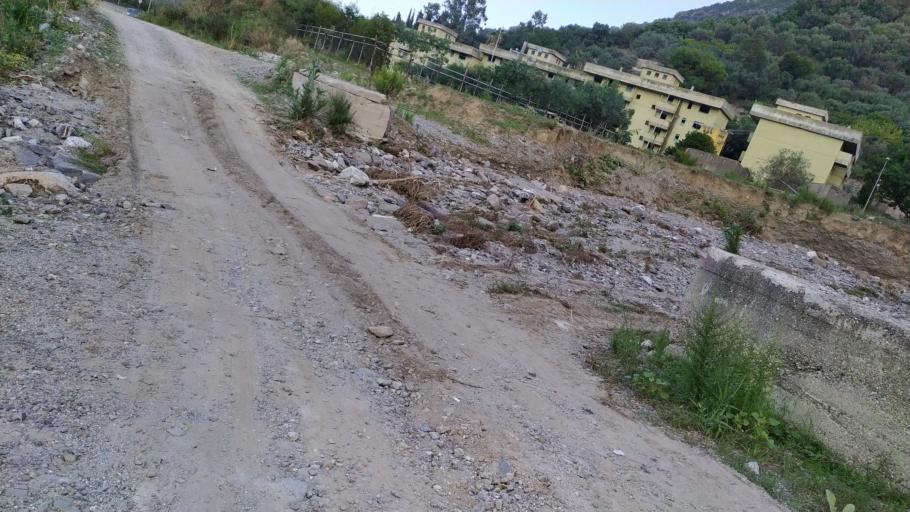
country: IT
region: Sicily
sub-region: Messina
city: Saponara
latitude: 38.1958
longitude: 15.4296
